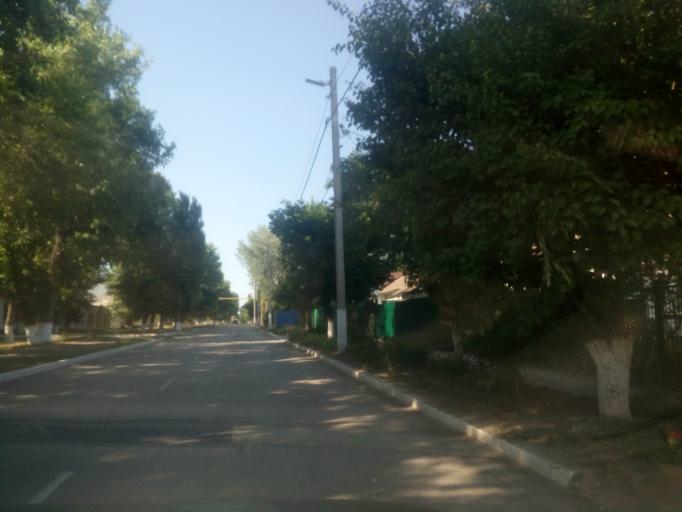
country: RU
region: Rostov
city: Sholokhovskiy
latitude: 48.2800
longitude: 41.0377
